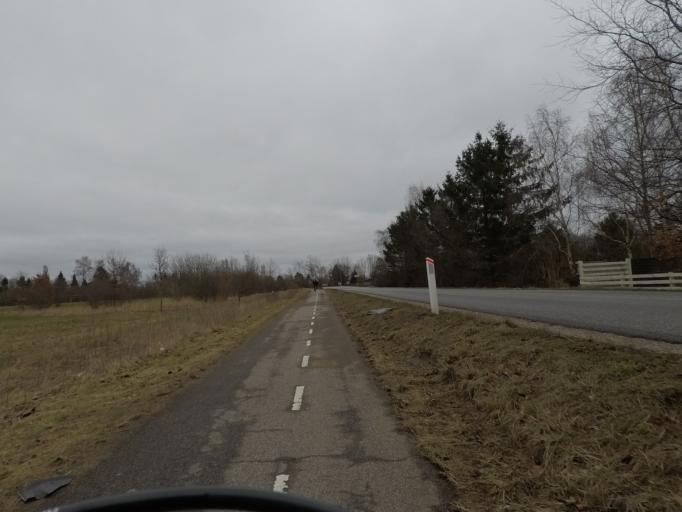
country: DK
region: Capital Region
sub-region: Egedal Kommune
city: Smorumnedre
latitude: 55.7187
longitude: 12.3207
